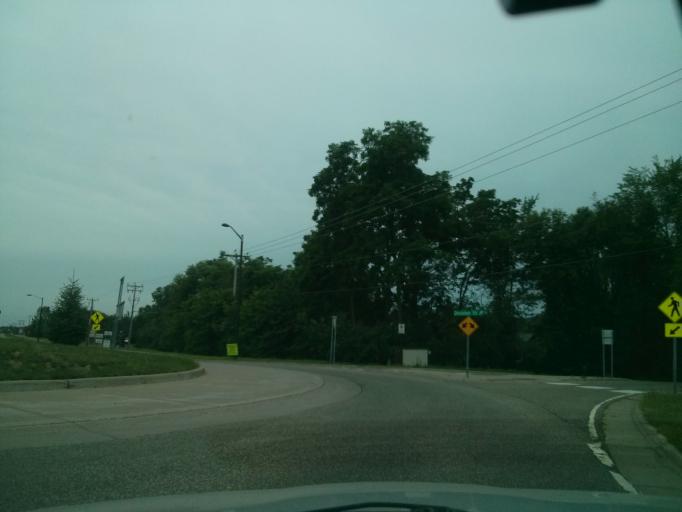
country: US
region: Minnesota
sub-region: Washington County
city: Lakeland
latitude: 44.9498
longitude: -92.7710
